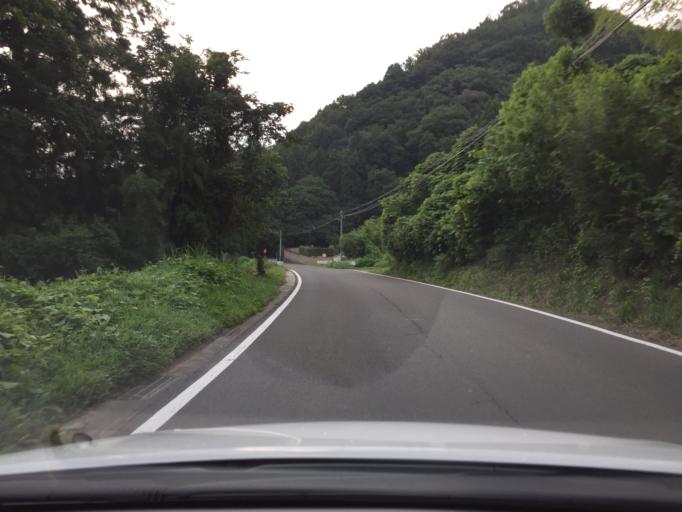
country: JP
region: Fukushima
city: Fukushima-shi
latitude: 37.7214
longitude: 140.4912
